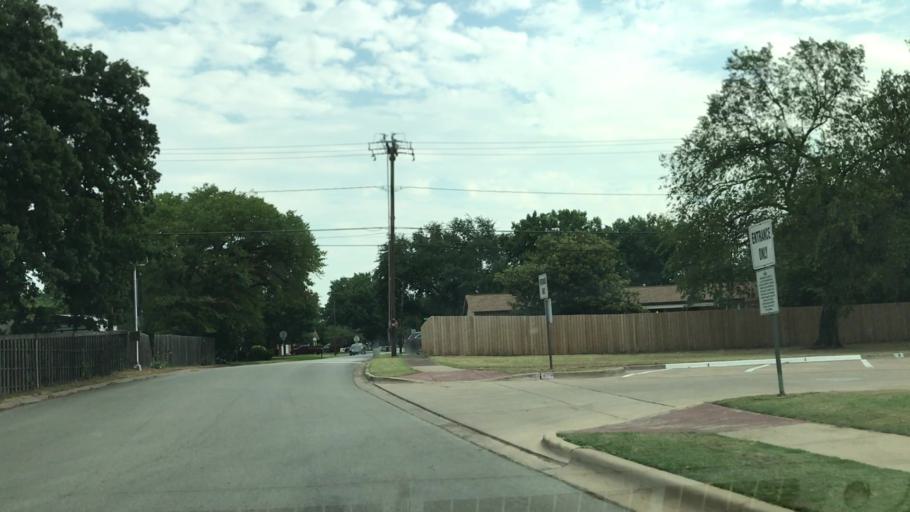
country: US
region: Texas
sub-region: Tarrant County
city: Hurst
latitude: 32.8269
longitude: -97.1700
